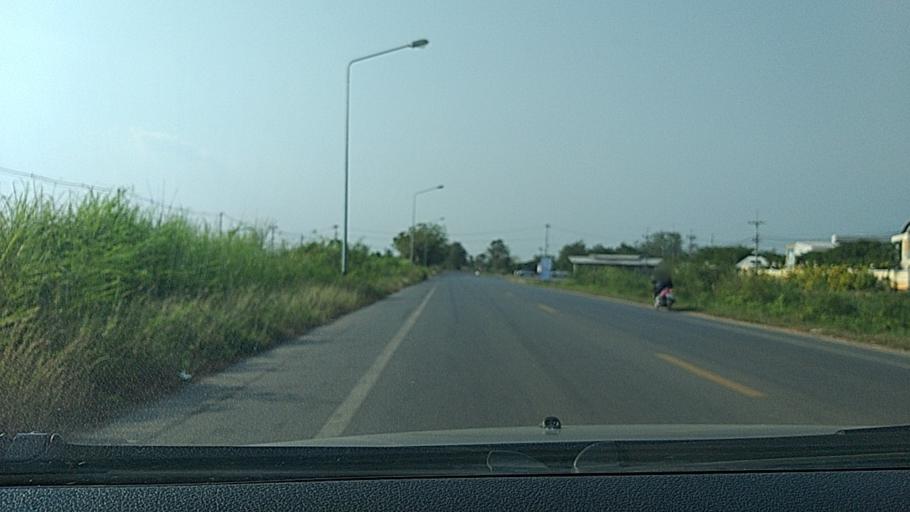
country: TH
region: Sing Buri
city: Phrom Buri
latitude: 14.8191
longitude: 100.4306
